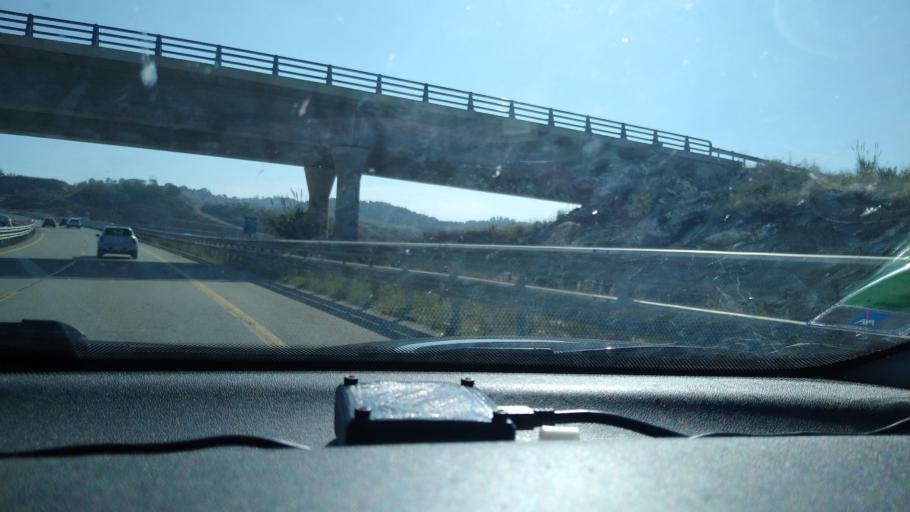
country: ES
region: Catalonia
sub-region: Provincia de Barcelona
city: Viladecavalls
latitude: 41.5563
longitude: 1.9751
